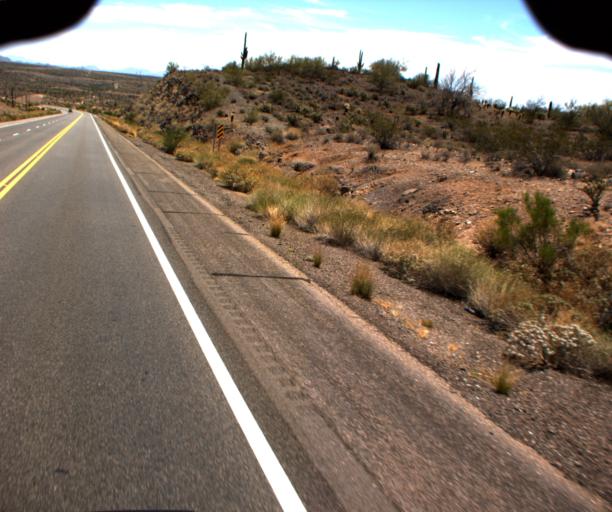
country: US
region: Arizona
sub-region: Maricopa County
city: Anthem
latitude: 33.8292
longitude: -112.2929
